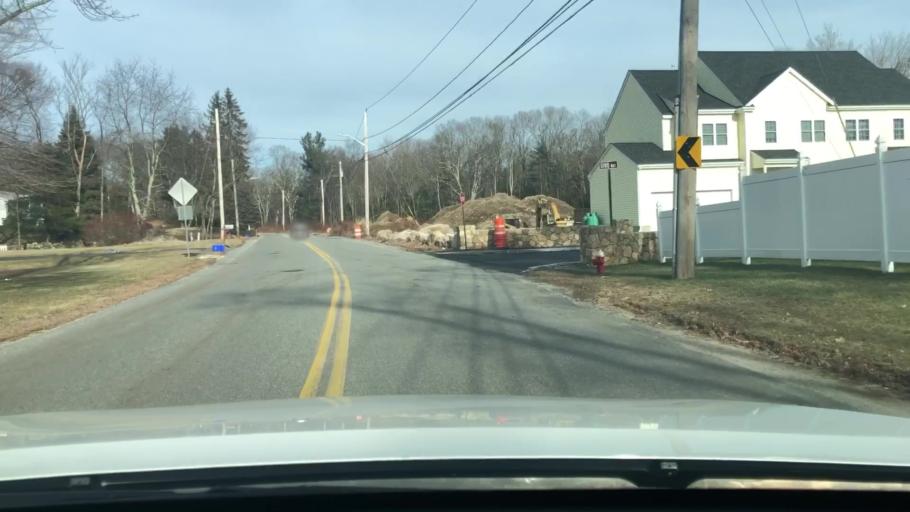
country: US
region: Massachusetts
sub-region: Worcester County
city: Milford
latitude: 42.1242
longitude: -71.4946
